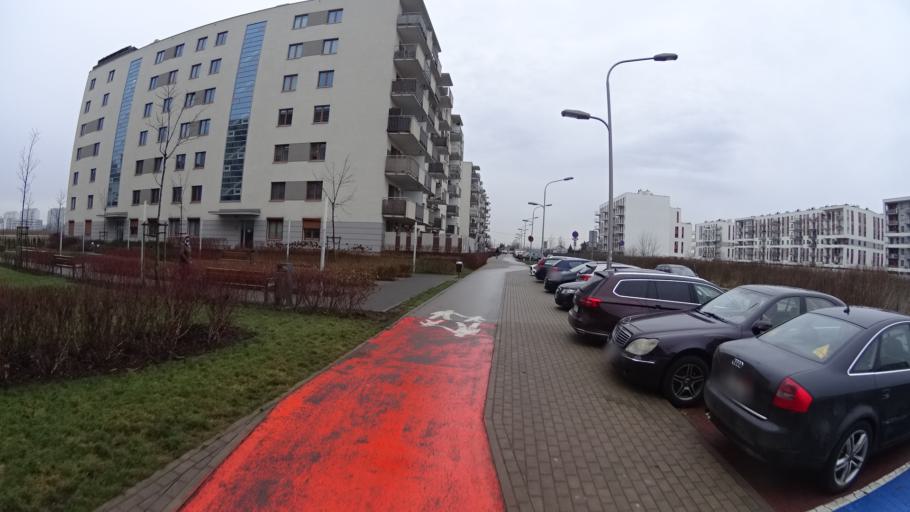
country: PL
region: Masovian Voivodeship
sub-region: Warszawa
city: Bemowo
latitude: 52.2293
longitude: 20.8906
